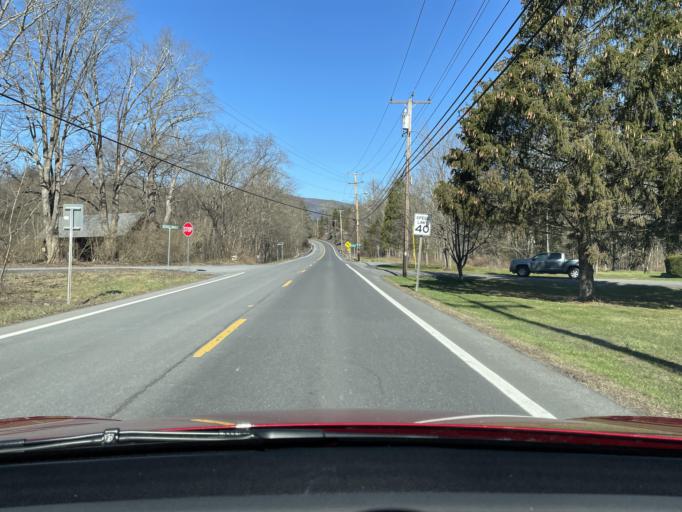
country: US
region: New York
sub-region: Ulster County
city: Saugerties
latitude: 42.0825
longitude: -74.0076
